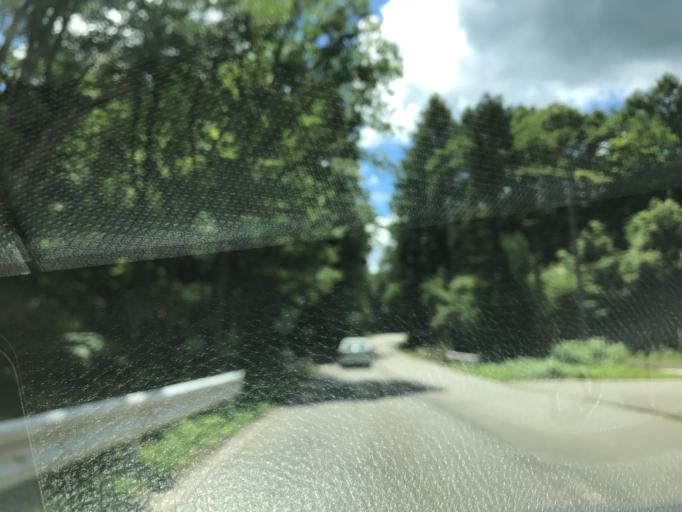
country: JP
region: Gifu
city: Takayama
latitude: 36.0692
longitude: 137.1073
